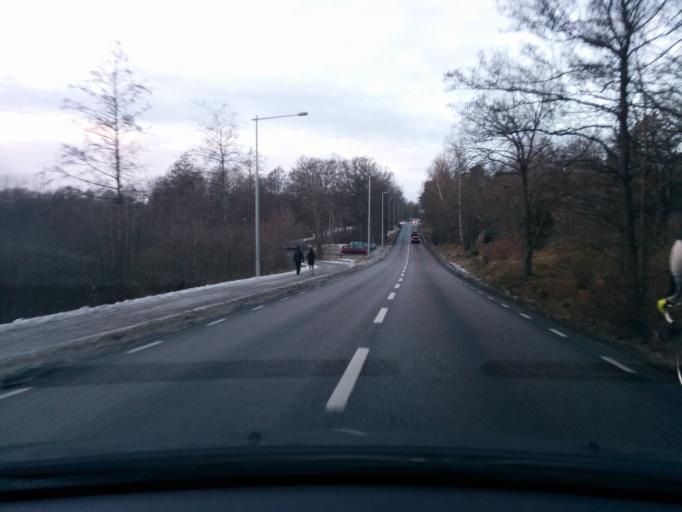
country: SE
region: Stockholm
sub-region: Nacka Kommun
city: Nacka
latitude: 59.2899
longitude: 18.1562
